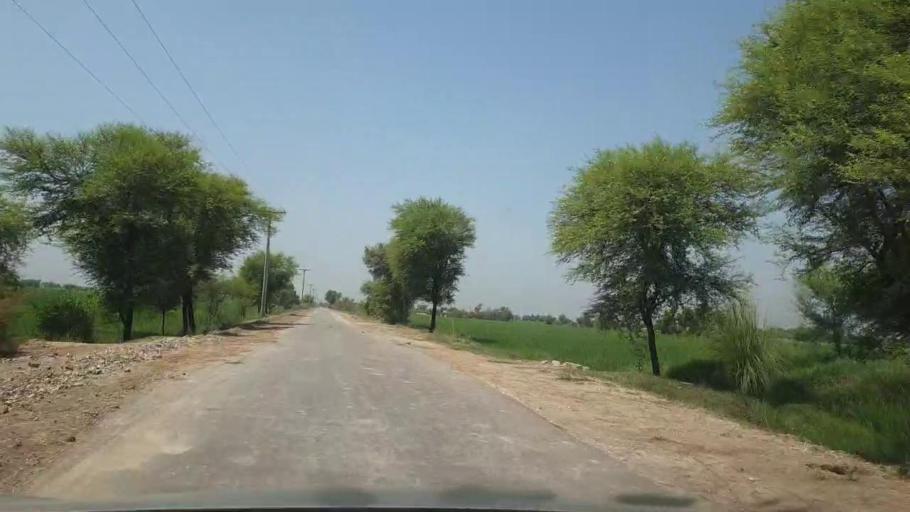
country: PK
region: Sindh
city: Warah
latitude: 27.4831
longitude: 67.7493
